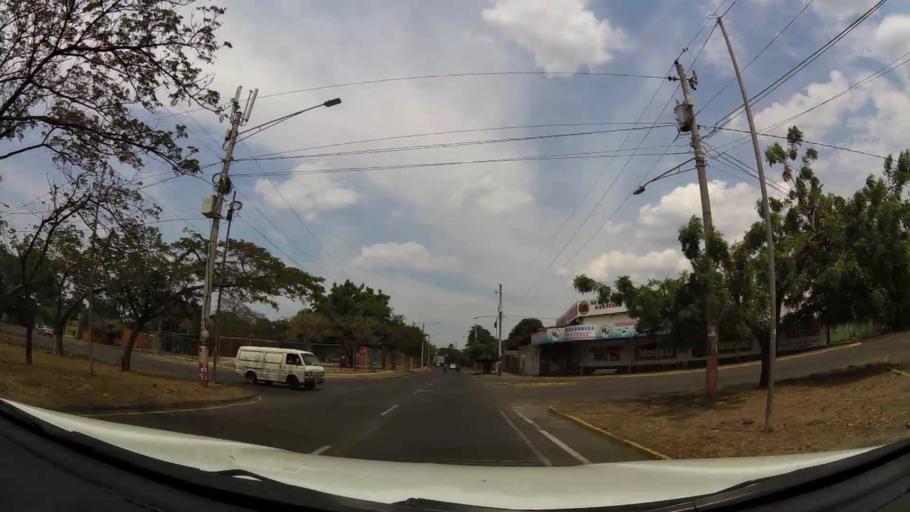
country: NI
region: Managua
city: Managua
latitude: 12.1554
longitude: -86.2856
